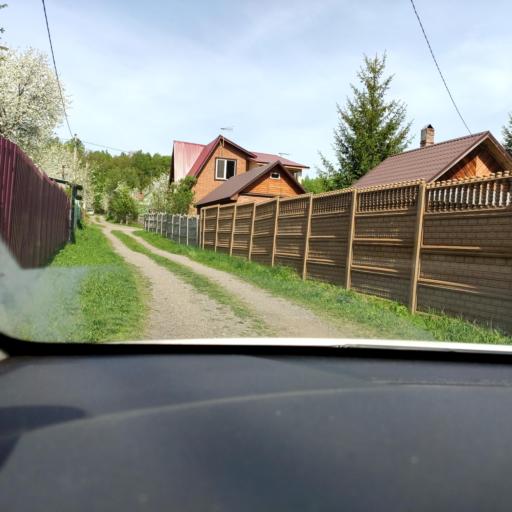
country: RU
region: Tatarstan
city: Osinovo
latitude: 55.7482
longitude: 48.8133
